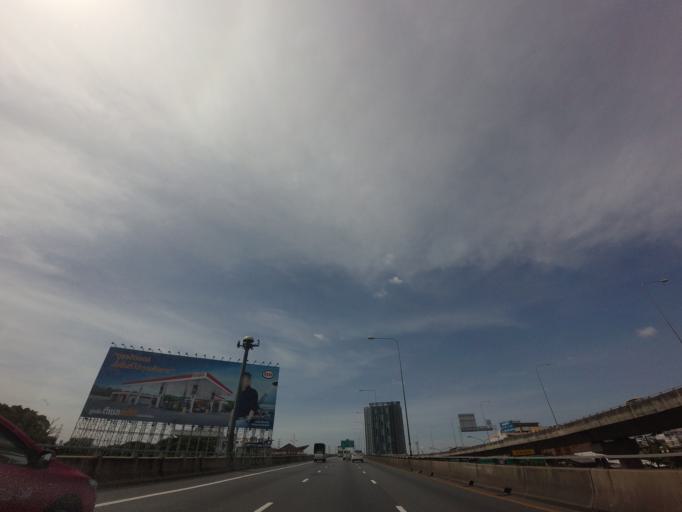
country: TH
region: Bangkok
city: Watthana
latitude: 13.7446
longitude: 100.6097
